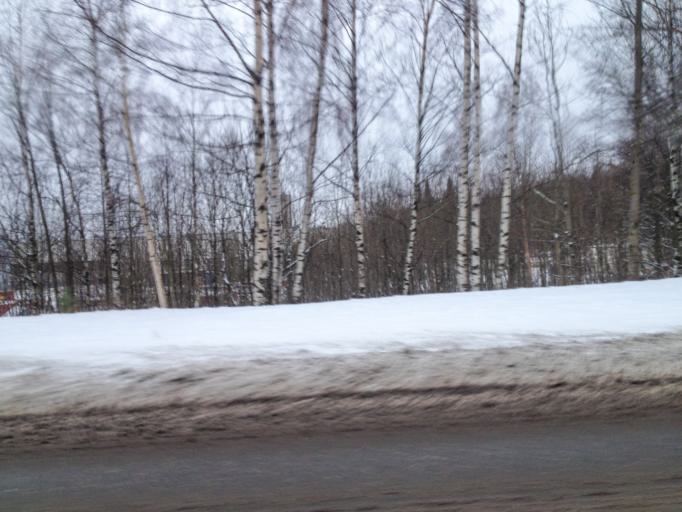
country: FI
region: Uusimaa
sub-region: Helsinki
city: Vantaa
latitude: 60.2143
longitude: 25.0593
